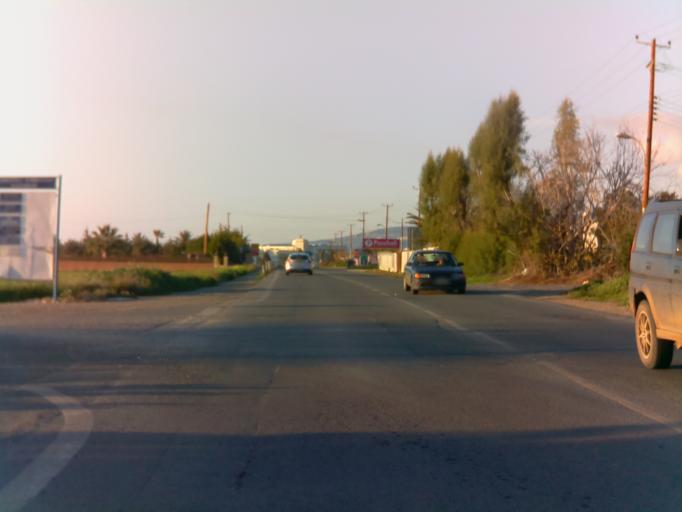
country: CY
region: Pafos
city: Chlorakas
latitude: 34.7997
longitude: 32.4001
